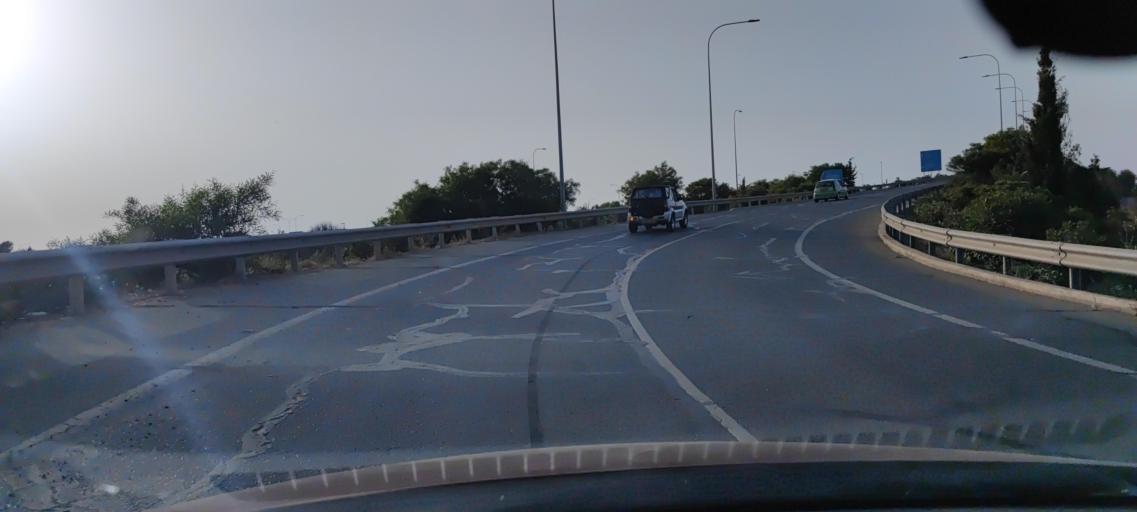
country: CY
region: Ammochostos
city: Liopetri
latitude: 34.9831
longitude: 33.9286
